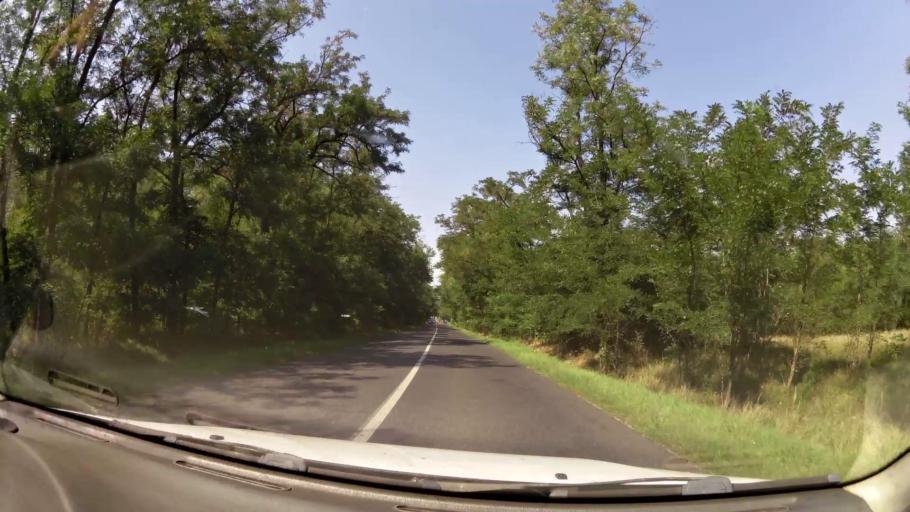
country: HU
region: Pest
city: Tapioszecso
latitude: 47.4354
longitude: 19.5990
